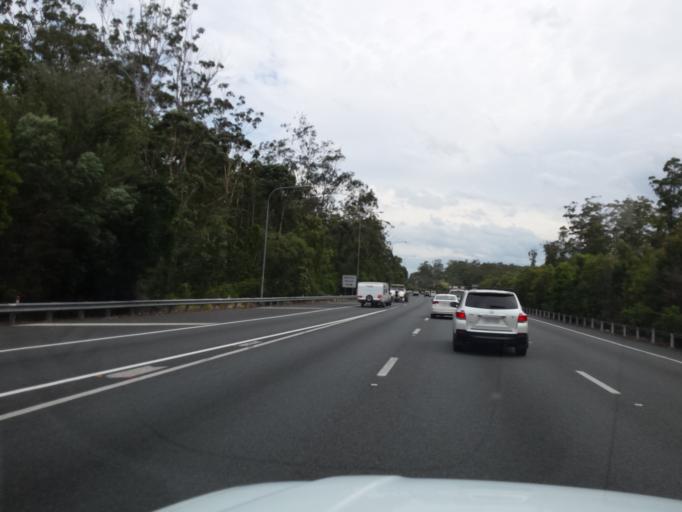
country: AU
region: Queensland
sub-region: Gold Coast
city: Nerang
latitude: -27.9605
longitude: 153.3453
